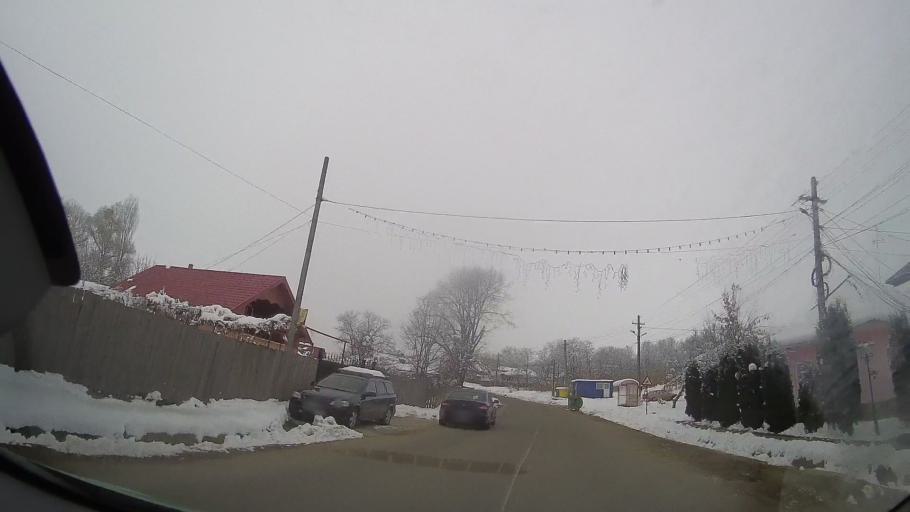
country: RO
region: Neamt
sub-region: Comuna Bozieni
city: Bozieni
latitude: 46.8341
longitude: 27.1620
